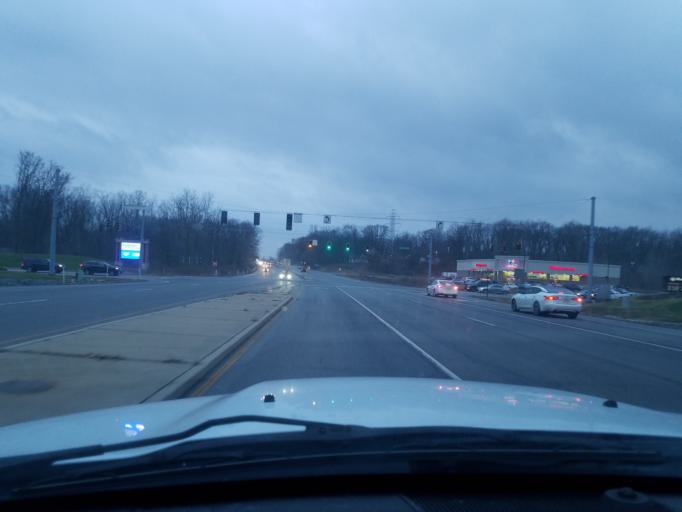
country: US
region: Indiana
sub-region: Huntington County
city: Roanoke
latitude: 41.0307
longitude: -85.2579
